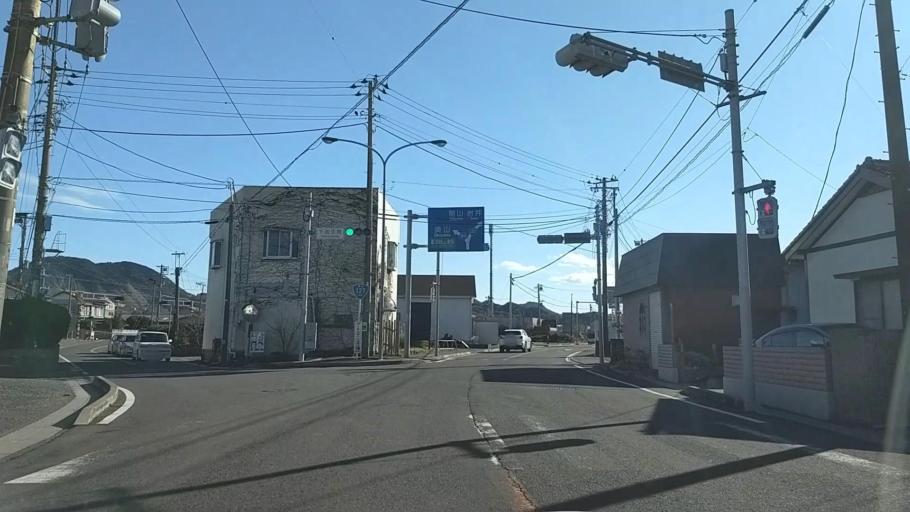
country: JP
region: Chiba
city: Tateyama
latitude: 35.1102
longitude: 139.8341
